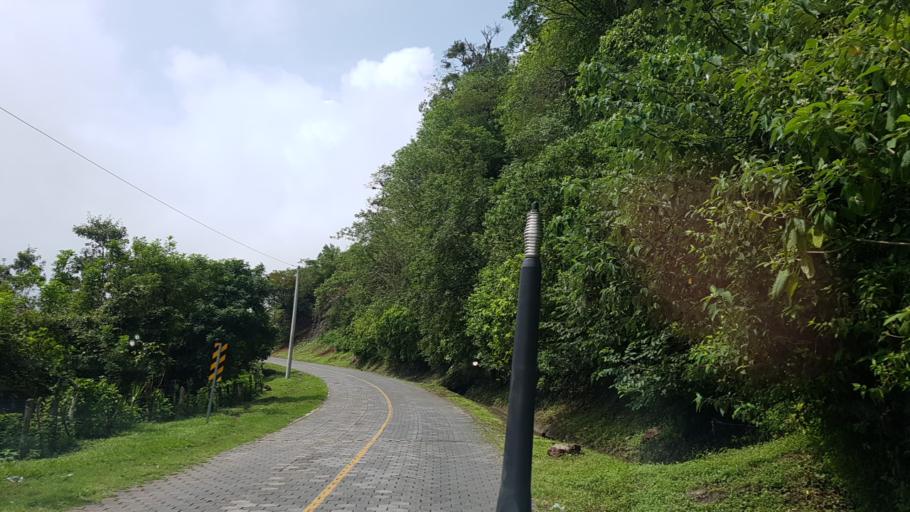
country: NI
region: Leon
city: Santa Rosa del Penon
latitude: 12.9380
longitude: -86.3387
